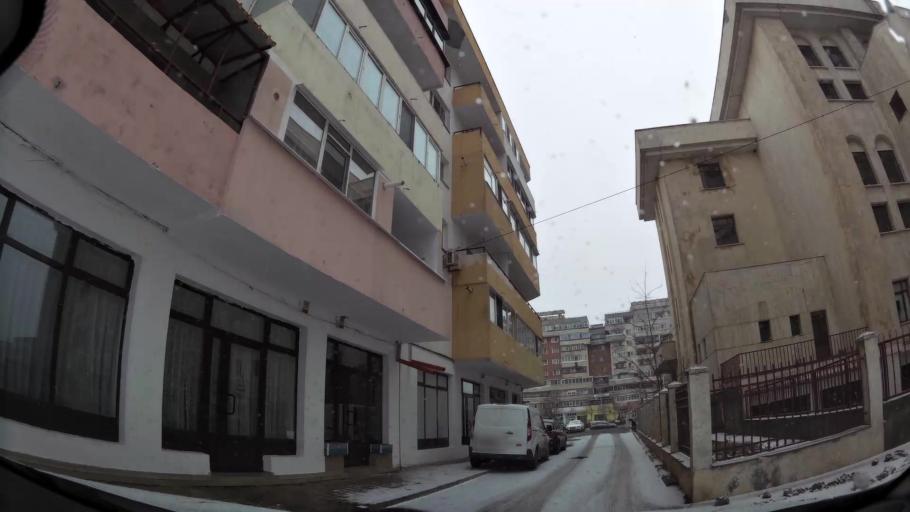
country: RO
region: Dambovita
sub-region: Municipiul Targoviste
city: Targoviste
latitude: 44.9209
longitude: 25.4774
